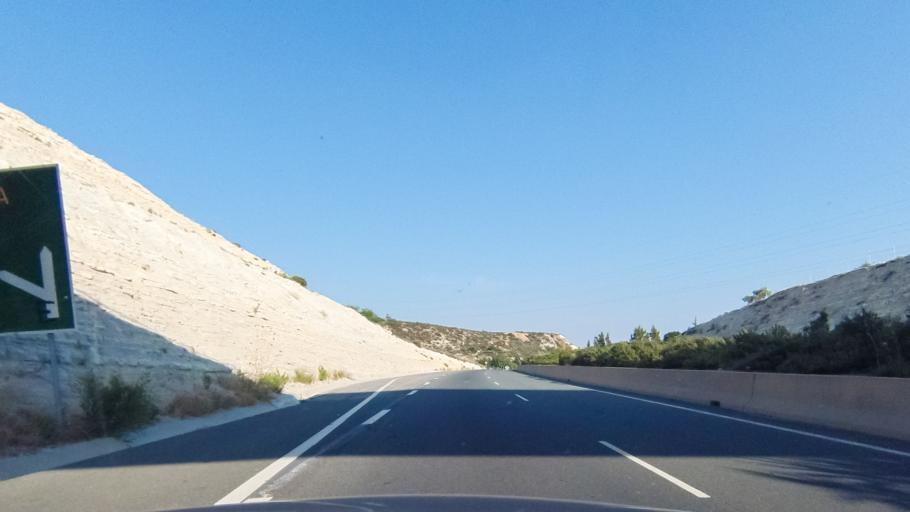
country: CY
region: Limassol
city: Sotira
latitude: 34.7019
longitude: 32.8577
